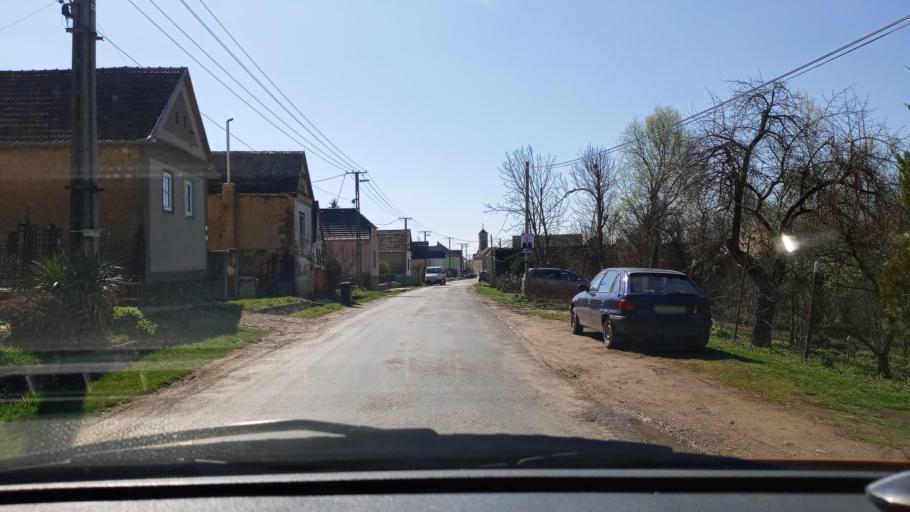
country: HU
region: Baranya
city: Kozarmisleny
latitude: 46.0615
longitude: 18.3743
